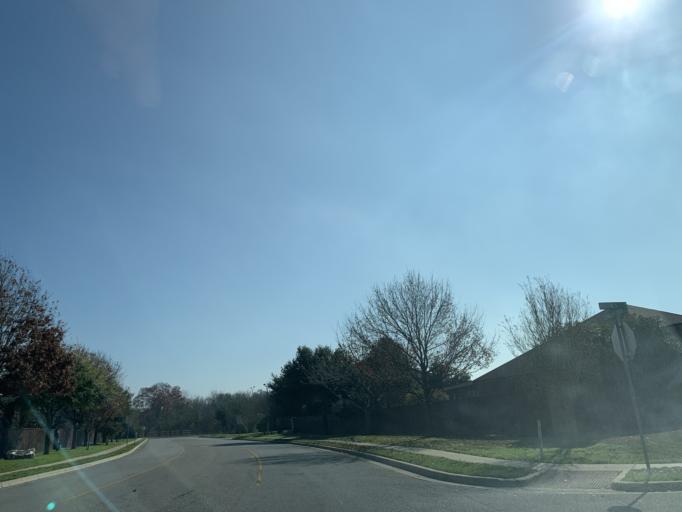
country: US
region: Texas
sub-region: Williamson County
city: Round Rock
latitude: 30.5296
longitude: -97.6416
